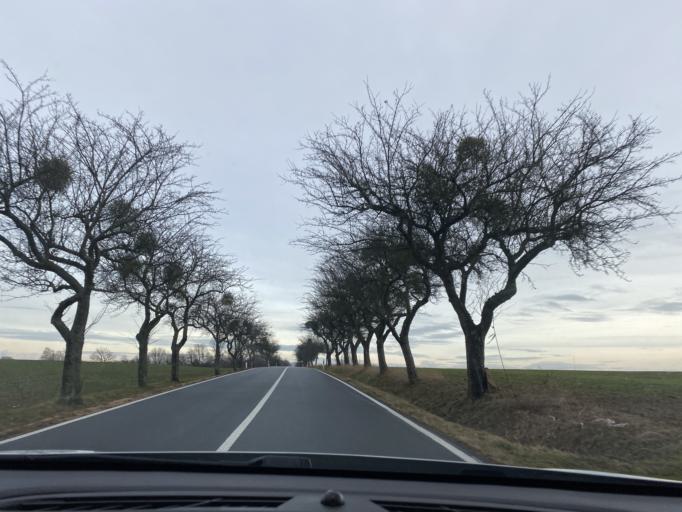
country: DE
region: Saxony
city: Reichenbach
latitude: 51.1459
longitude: 14.7848
